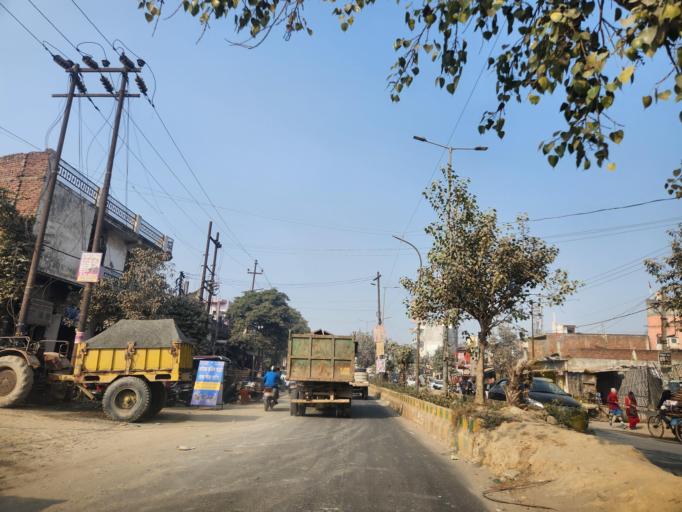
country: IN
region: Uttar Pradesh
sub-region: Ghaziabad
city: Ghaziabad
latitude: 28.6768
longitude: 77.4167
